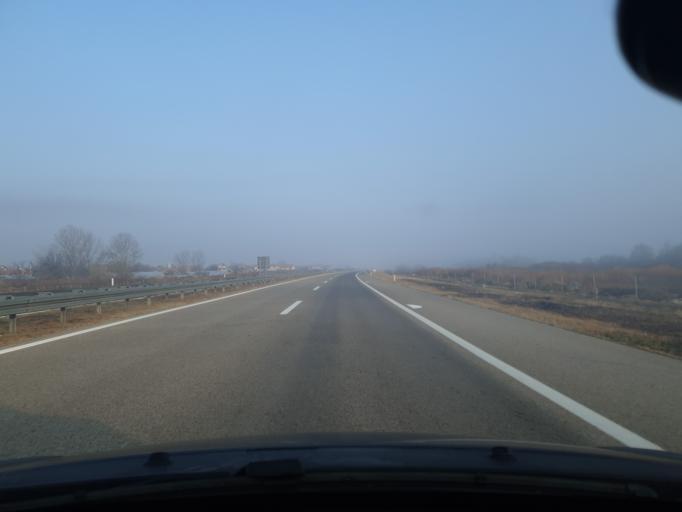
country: RS
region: Central Serbia
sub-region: Jablanicki Okrug
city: Leskovac
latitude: 42.9845
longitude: 22.0291
